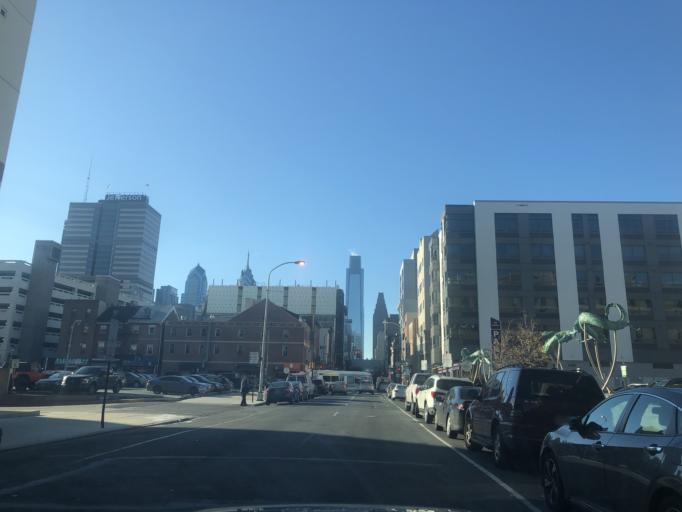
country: US
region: Pennsylvania
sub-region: Philadelphia County
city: Philadelphia
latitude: 39.9532
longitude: -75.1536
